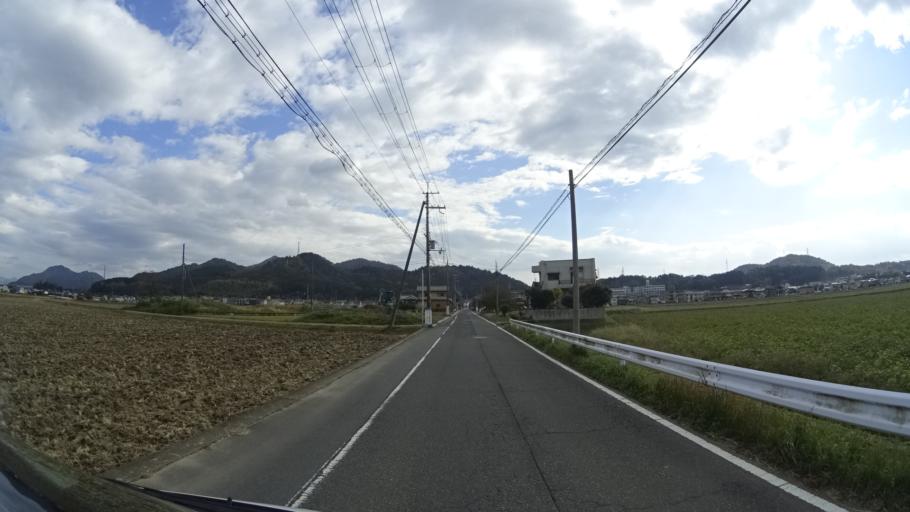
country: JP
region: Kyoto
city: Fukuchiyama
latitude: 35.3055
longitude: 135.1764
